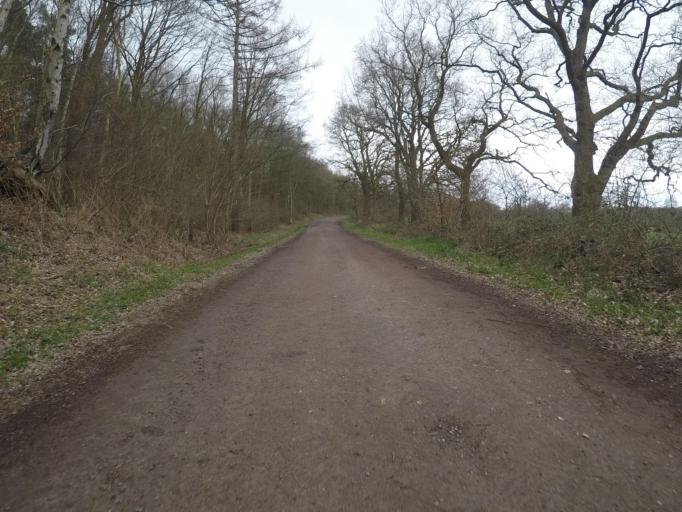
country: DE
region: Lower Saxony
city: Langen
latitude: 53.6044
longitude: 8.6682
